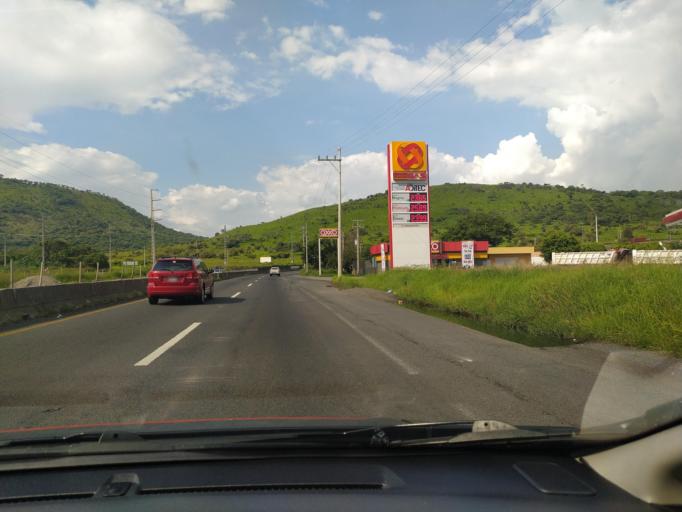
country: MX
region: Jalisco
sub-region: Acatlan de Juarez
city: Villa de los Ninos
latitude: 20.4333
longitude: -103.5794
